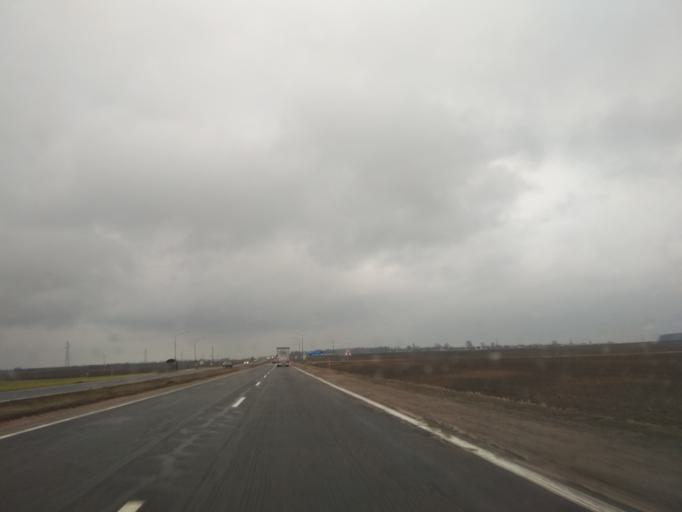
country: BY
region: Minsk
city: Dukora
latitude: 53.6442
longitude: 27.9886
